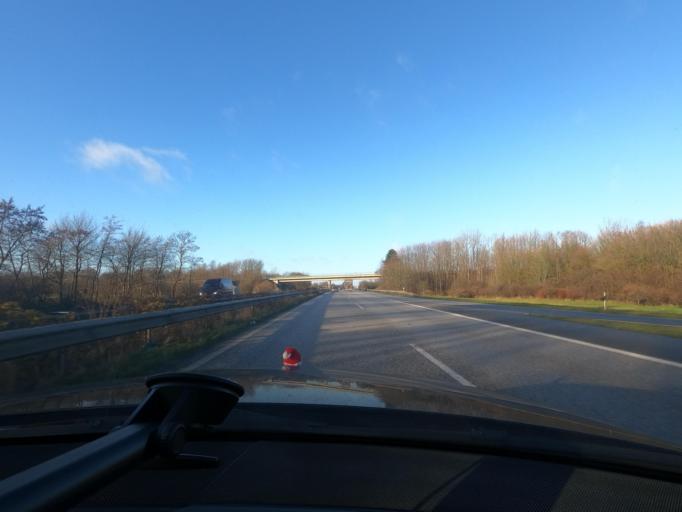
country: DE
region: Schleswig-Holstein
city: Busdorf
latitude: 54.4815
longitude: 9.5356
